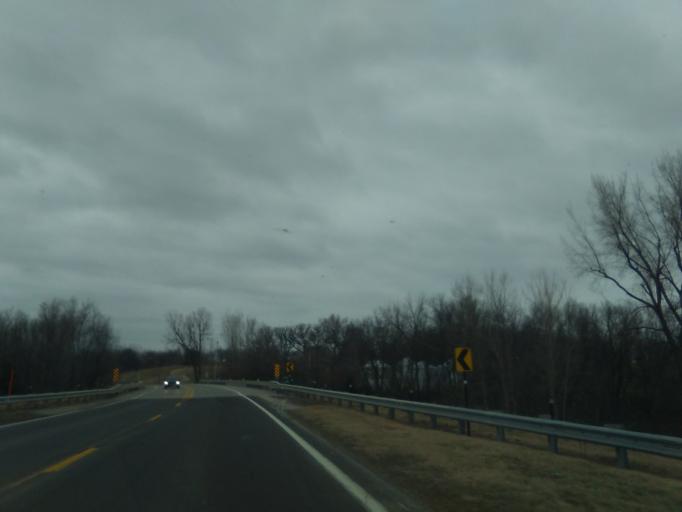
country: US
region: Nebraska
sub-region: Richardson County
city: Falls City
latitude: 40.0550
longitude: -95.4358
